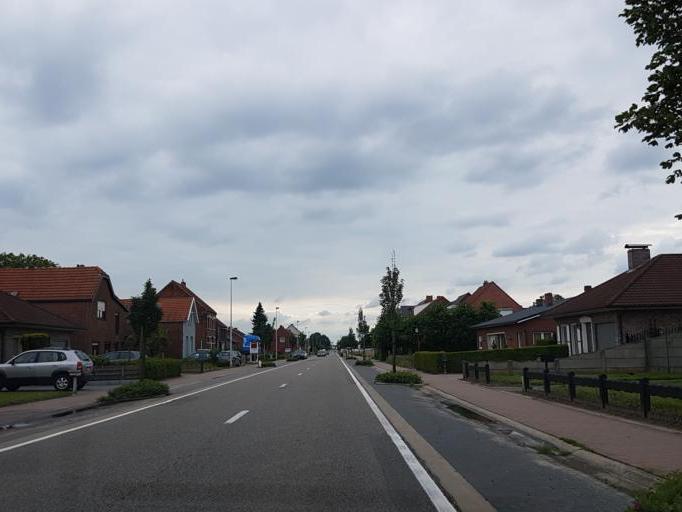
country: BE
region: Flanders
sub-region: Provincie Antwerpen
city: Rijkevorsel
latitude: 51.3369
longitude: 4.7514
